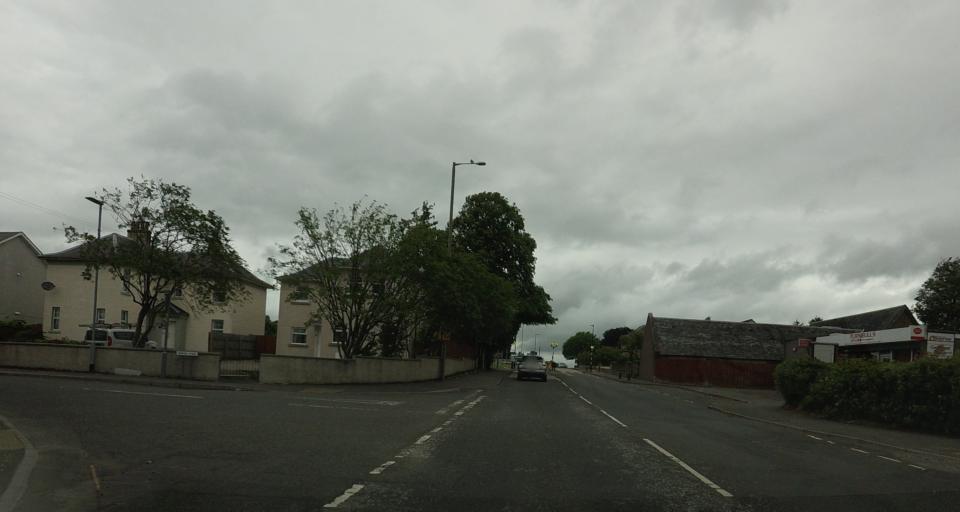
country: GB
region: Scotland
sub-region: Stirling
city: Bannockburn
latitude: 56.0920
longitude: -3.9328
